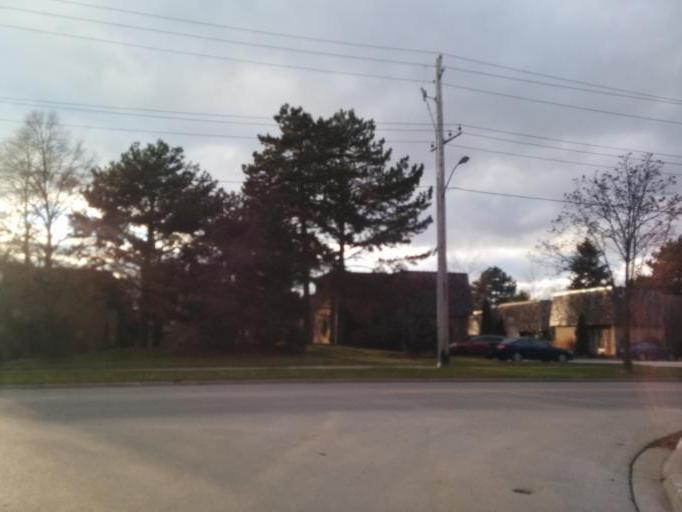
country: CA
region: Ontario
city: Etobicoke
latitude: 43.6423
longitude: -79.5860
